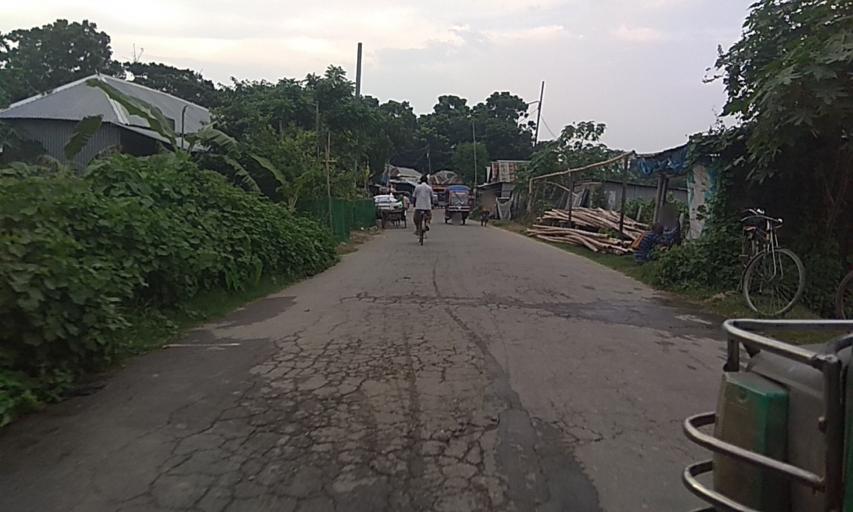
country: BD
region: Dhaka
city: Dohar
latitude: 23.4561
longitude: 90.0058
